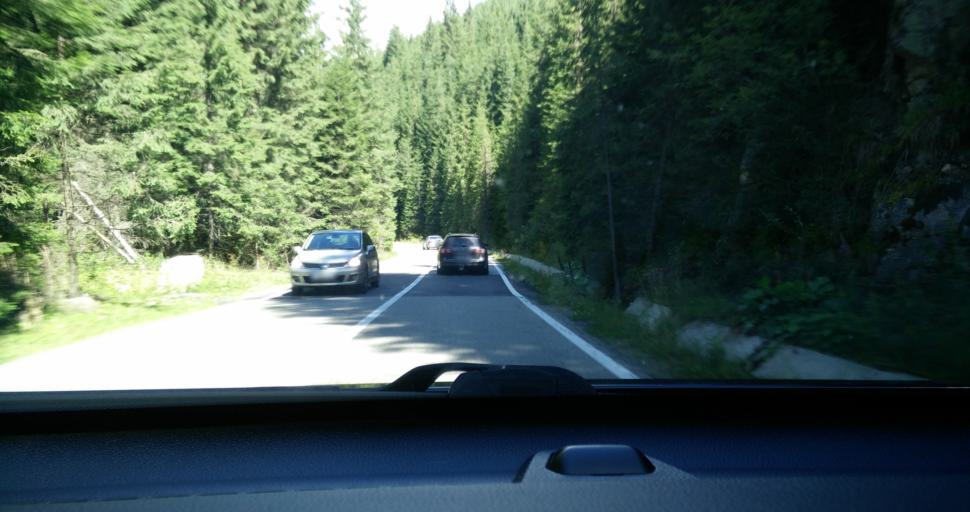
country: RO
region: Alba
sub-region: Comuna Sugag
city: Sugag
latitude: 45.5317
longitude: 23.6433
